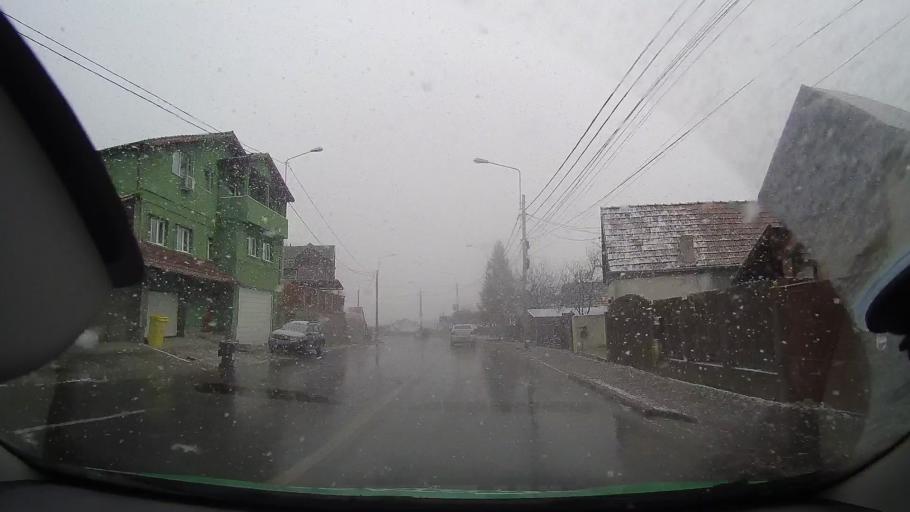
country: RO
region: Sibiu
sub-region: Municipiul Medias
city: Medias
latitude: 46.1727
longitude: 24.3399
